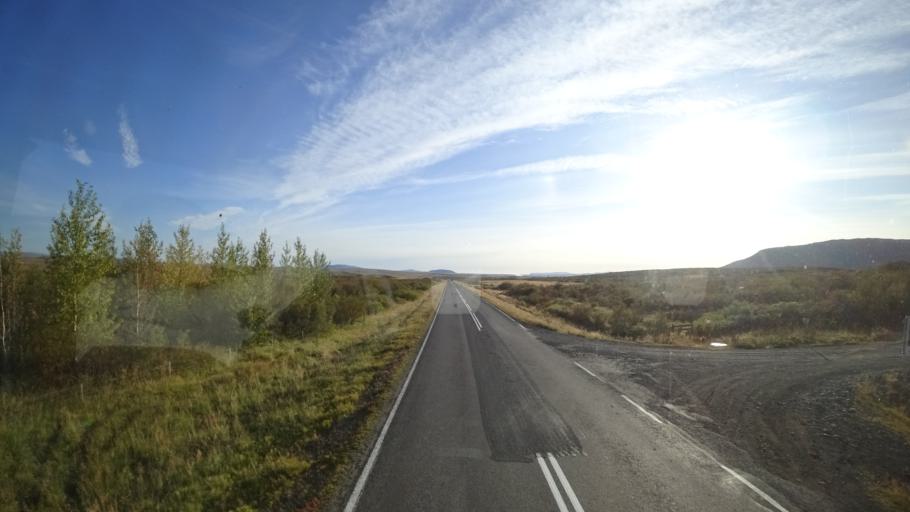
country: IS
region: South
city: Selfoss
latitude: 64.2642
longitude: -20.4683
